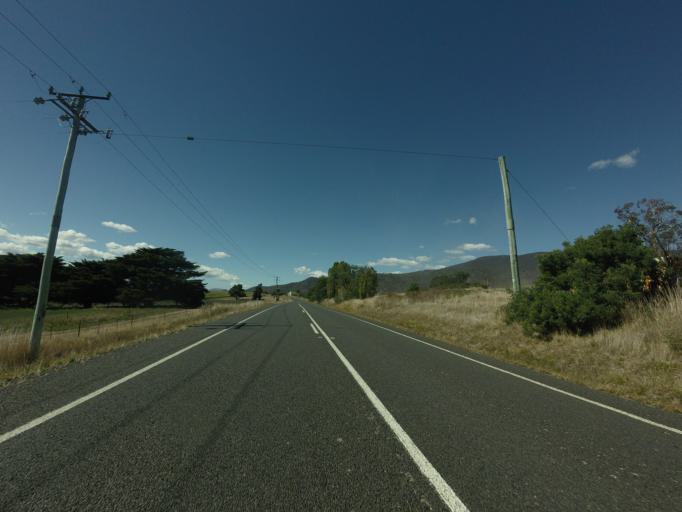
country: AU
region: Tasmania
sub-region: Break O'Day
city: St Helens
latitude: -41.7210
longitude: 147.8288
